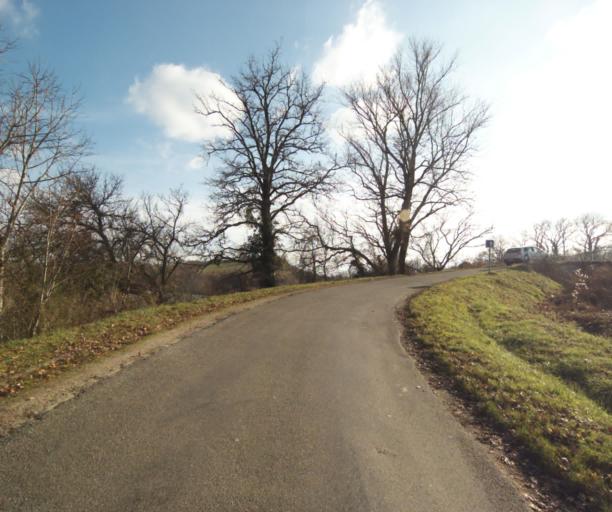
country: FR
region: Midi-Pyrenees
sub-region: Departement du Tarn-et-Garonne
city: Moissac
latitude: 44.1204
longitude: 1.0468
